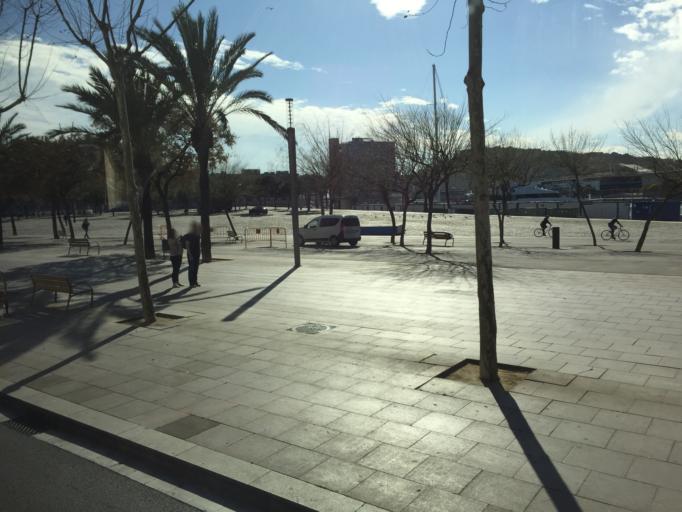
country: ES
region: Catalonia
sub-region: Provincia de Barcelona
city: Ciutat Vella
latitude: 41.3774
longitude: 2.1883
